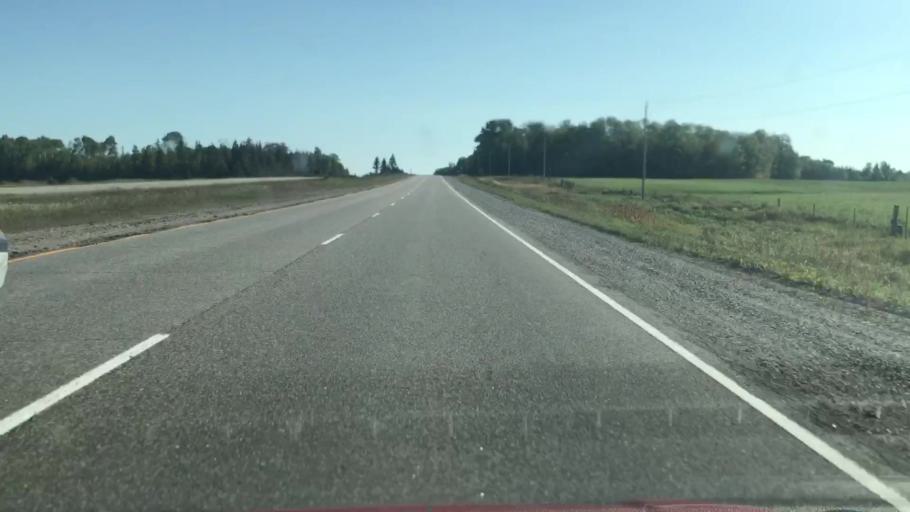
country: US
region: Michigan
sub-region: Chippewa County
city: Sault Ste. Marie
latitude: 46.3516
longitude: -84.0679
